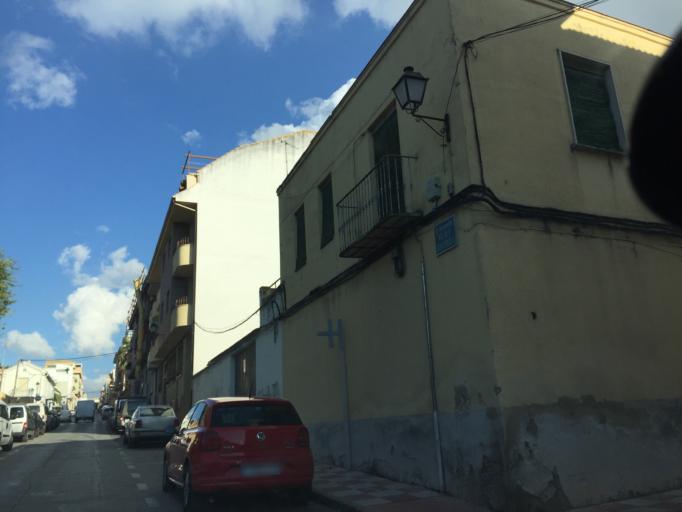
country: ES
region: Andalusia
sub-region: Provincia de Jaen
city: Mancha Real
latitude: 37.7878
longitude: -3.6104
